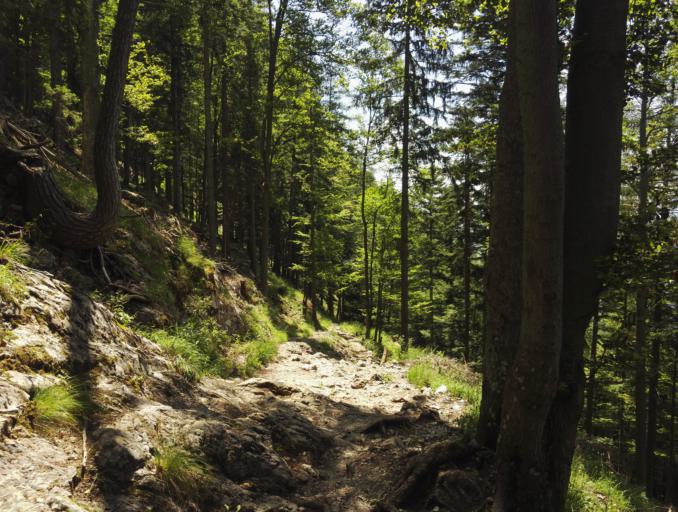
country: AT
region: Styria
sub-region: Politischer Bezirk Graz-Umgebung
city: Rothelstein
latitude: 47.3471
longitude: 15.3992
